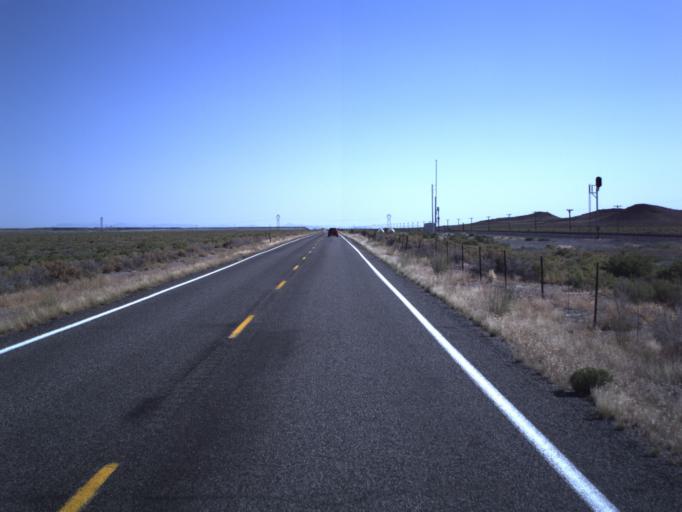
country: US
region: Utah
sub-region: Millard County
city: Delta
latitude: 39.1404
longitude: -112.7253
